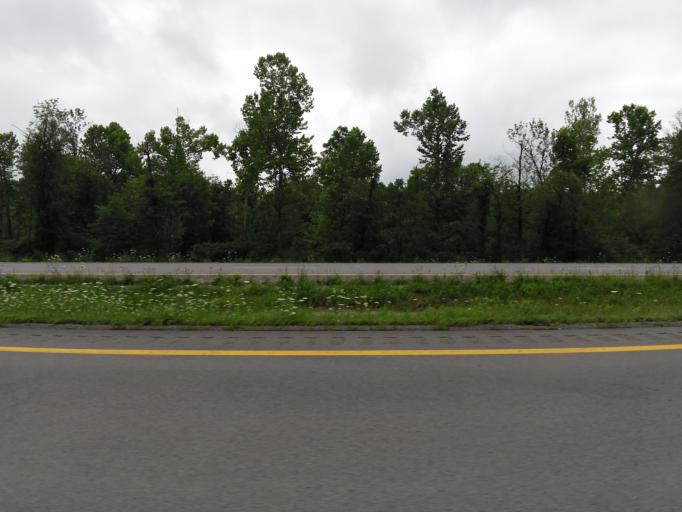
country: US
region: Kentucky
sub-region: Grayson County
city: Leitchfield
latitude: 37.4120
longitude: -86.4306
